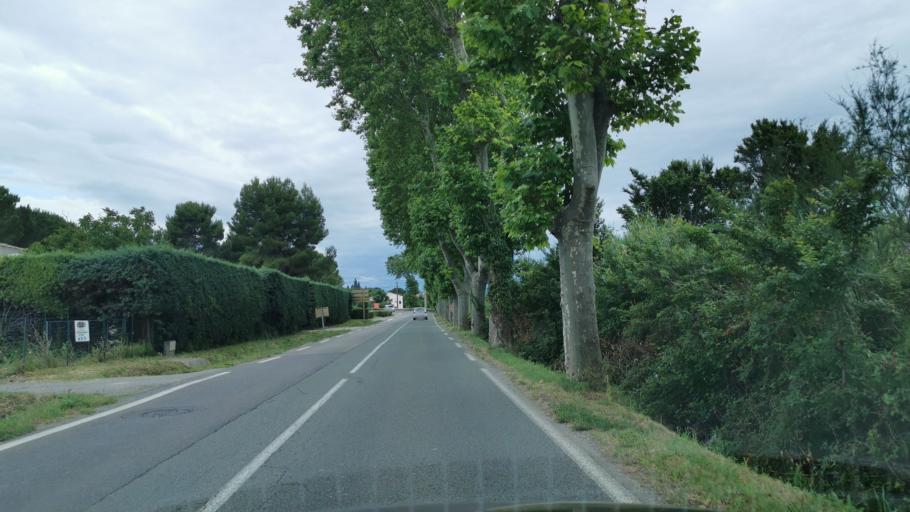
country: FR
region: Languedoc-Roussillon
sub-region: Departement de l'Aude
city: Marcorignan
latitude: 43.2317
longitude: 2.9253
